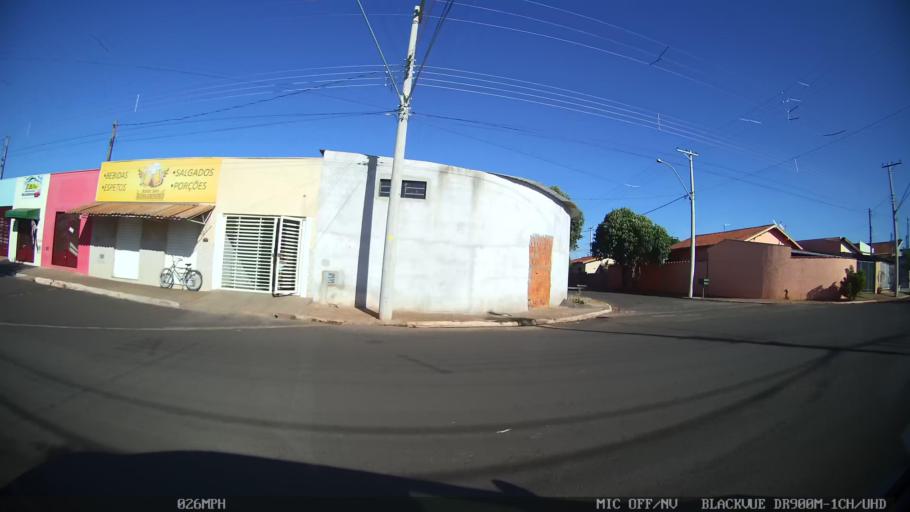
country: BR
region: Sao Paulo
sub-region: Olimpia
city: Olimpia
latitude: -20.7267
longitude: -48.8991
